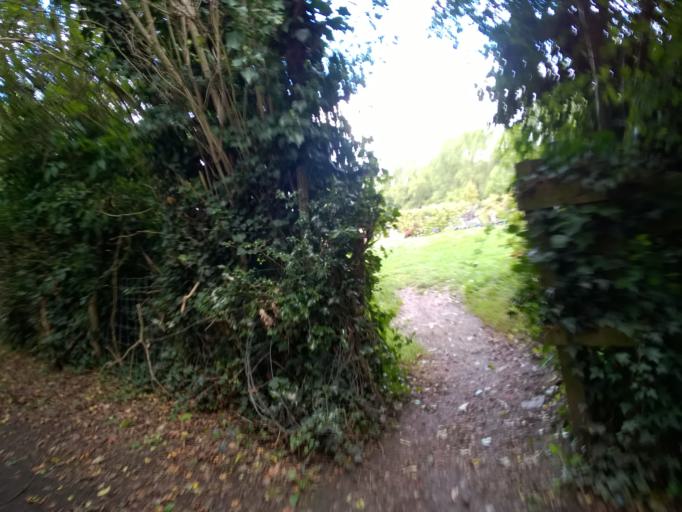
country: GB
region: England
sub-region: Leicestershire
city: Anstey
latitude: 52.6545
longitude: -1.1669
